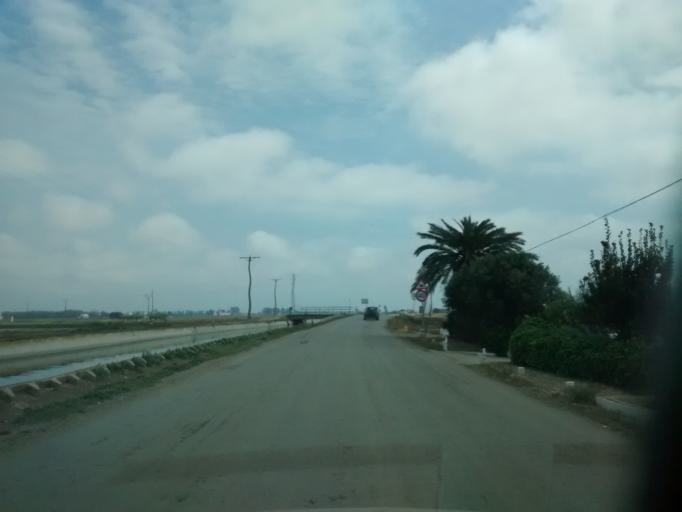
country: ES
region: Catalonia
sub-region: Provincia de Tarragona
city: Deltebre
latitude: 40.7024
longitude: 0.7393
